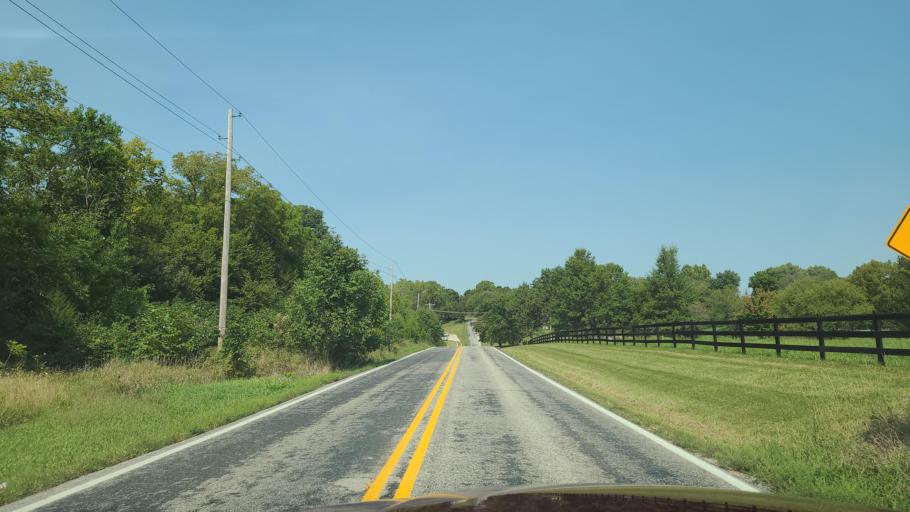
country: US
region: Kansas
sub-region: Douglas County
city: Lawrence
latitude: 38.9842
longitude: -95.2976
